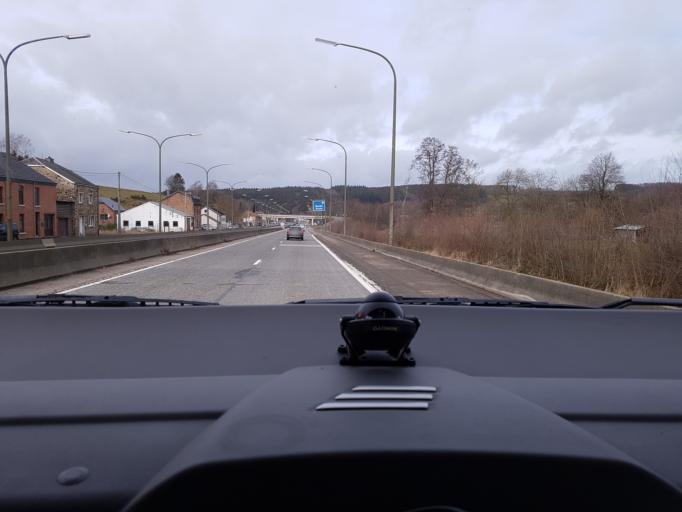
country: BE
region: Wallonia
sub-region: Province du Luxembourg
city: Nassogne
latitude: 50.1579
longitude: 5.4123
